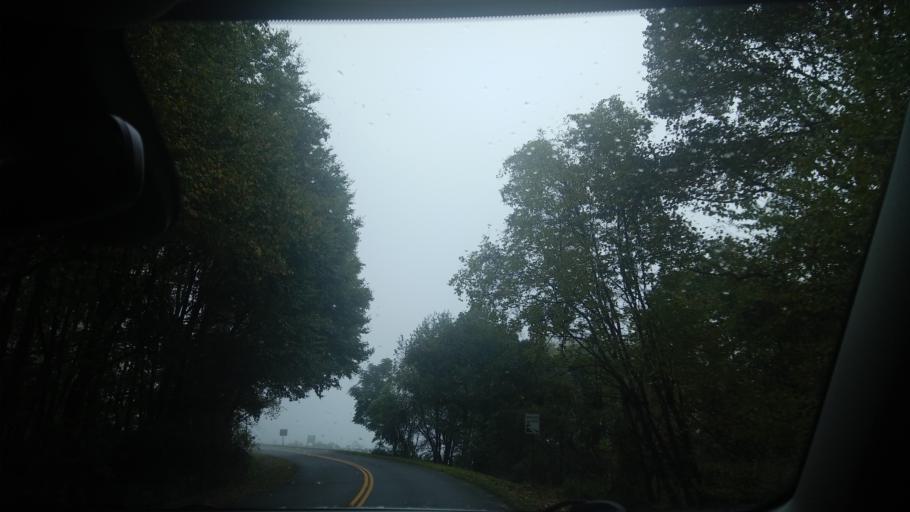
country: US
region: North Carolina
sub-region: Mitchell County
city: Spruce Pine
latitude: 35.8777
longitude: -81.9916
